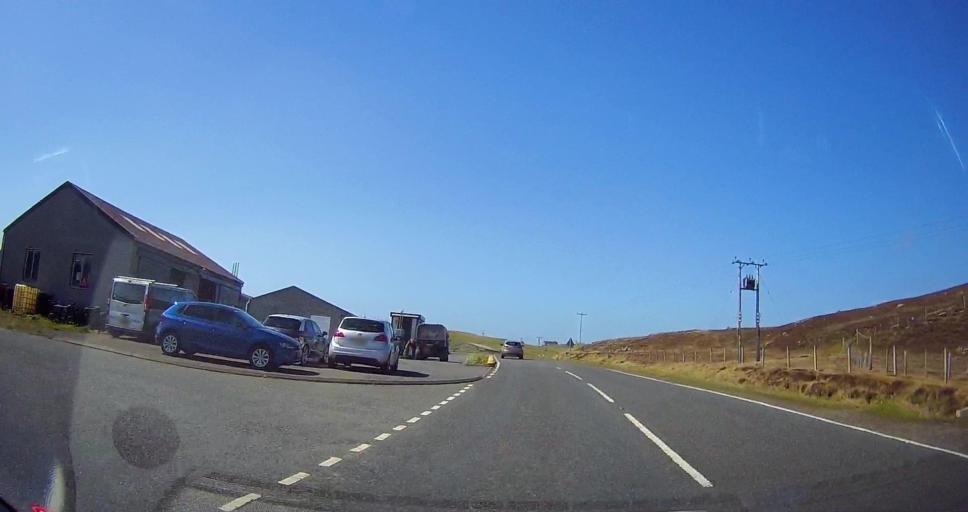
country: GB
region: Scotland
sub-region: Shetland Islands
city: Sandwick
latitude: 60.1052
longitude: -1.3108
